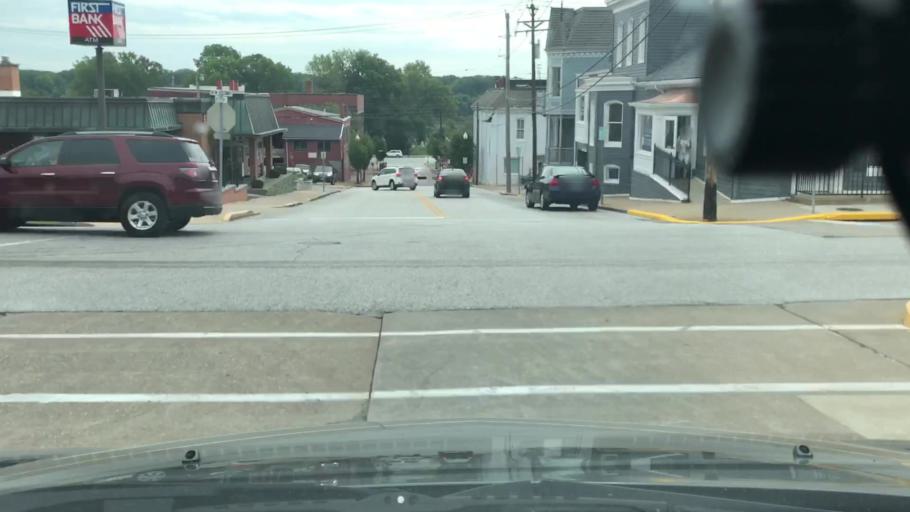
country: US
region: Missouri
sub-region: Saint Charles County
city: Saint Charles
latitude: 38.7816
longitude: -90.4827
